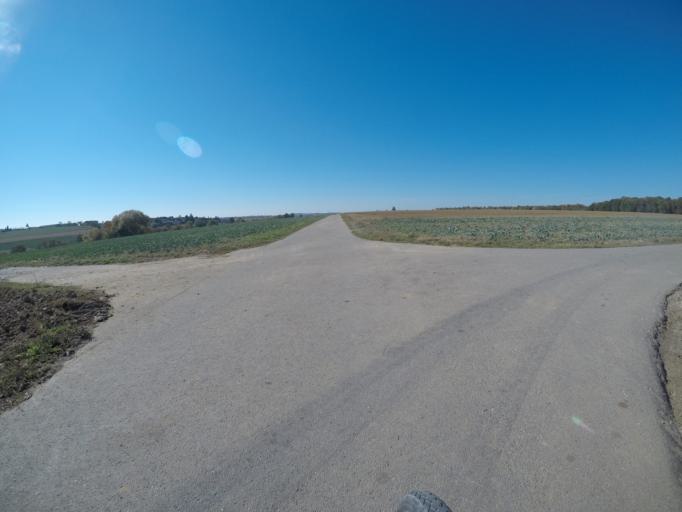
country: DE
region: Baden-Wuerttemberg
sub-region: Regierungsbezirk Stuttgart
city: Bondorf
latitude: 48.5368
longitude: 8.8749
